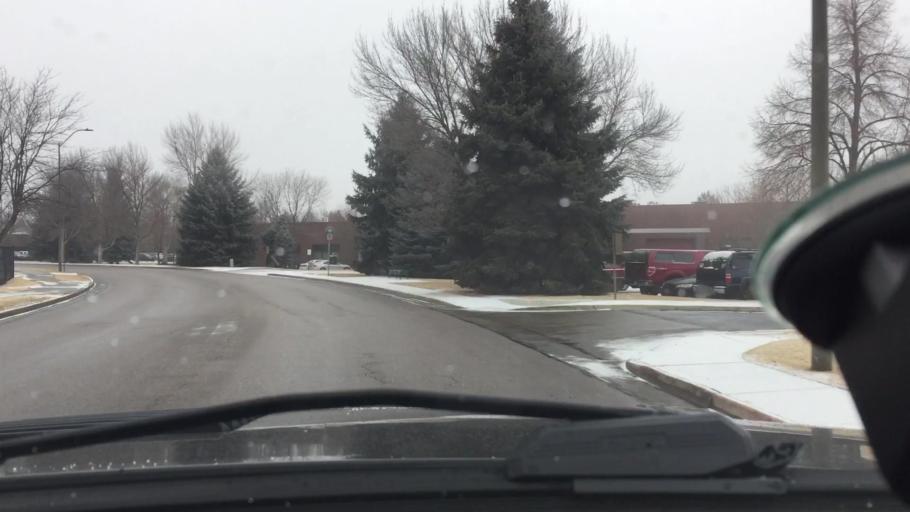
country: US
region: Colorado
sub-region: Larimer County
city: Fort Collins
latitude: 40.5646
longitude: -105.0323
